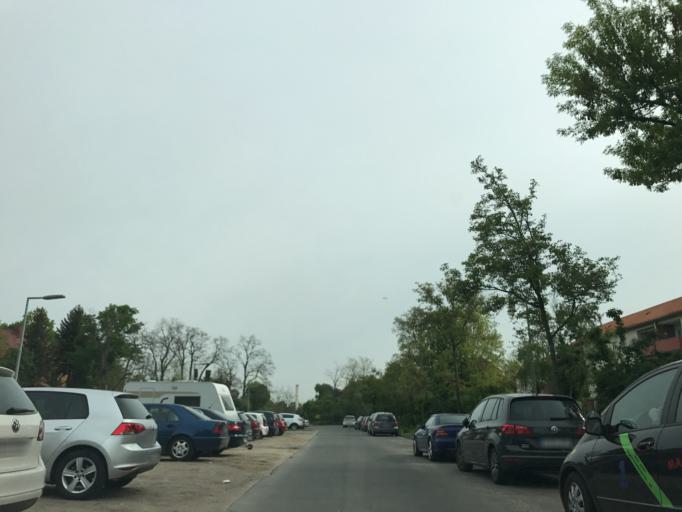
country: DE
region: Berlin
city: Wilhelmstadt
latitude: 52.5243
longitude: 13.1821
